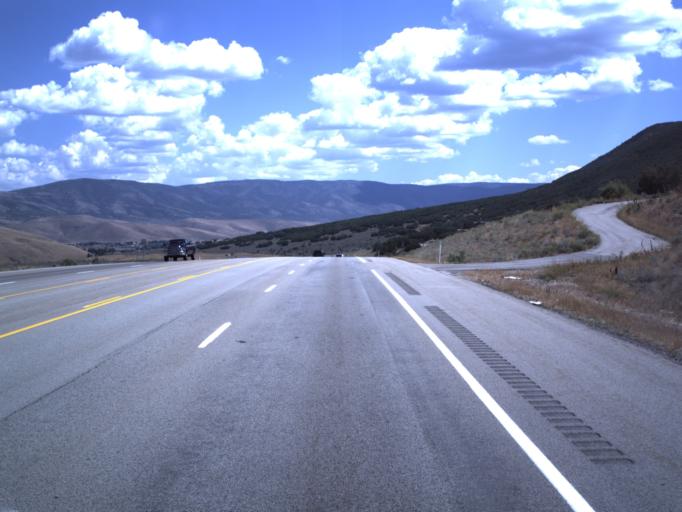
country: US
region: Utah
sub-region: Wasatch County
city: Midway
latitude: 40.4100
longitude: -111.5056
